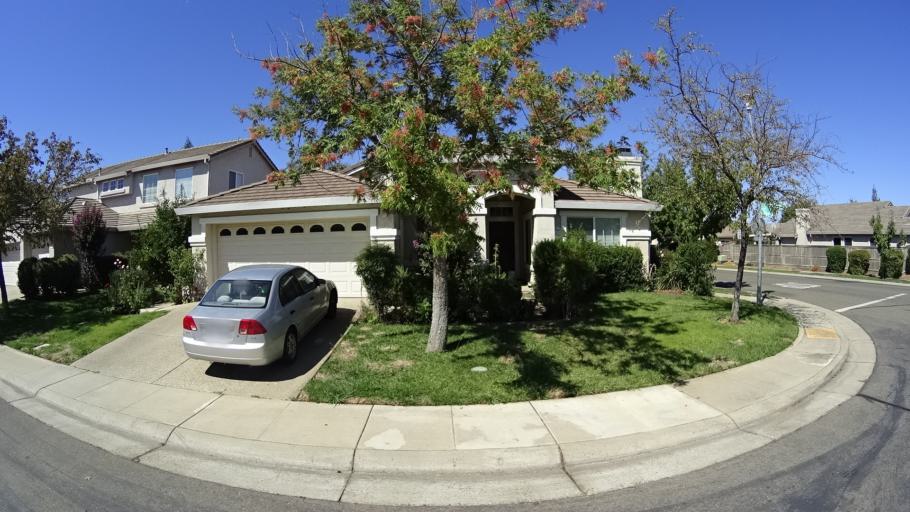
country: US
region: California
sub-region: Sacramento County
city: Elk Grove
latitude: 38.4069
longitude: -121.3462
